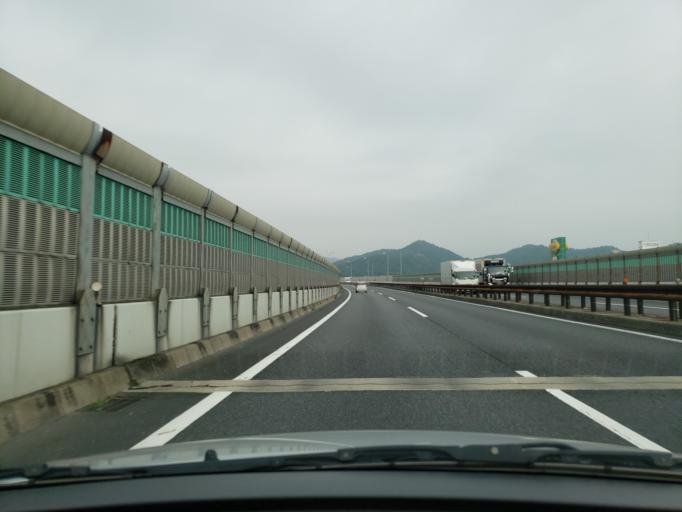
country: JP
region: Hyogo
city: Himeji
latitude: 34.8163
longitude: 134.6687
